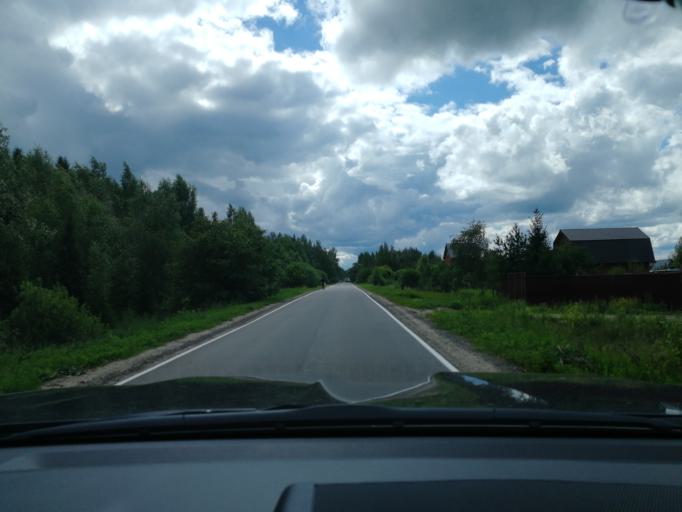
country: RU
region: Moskovskaya
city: Proletarskiy
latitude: 55.0135
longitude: 37.4857
